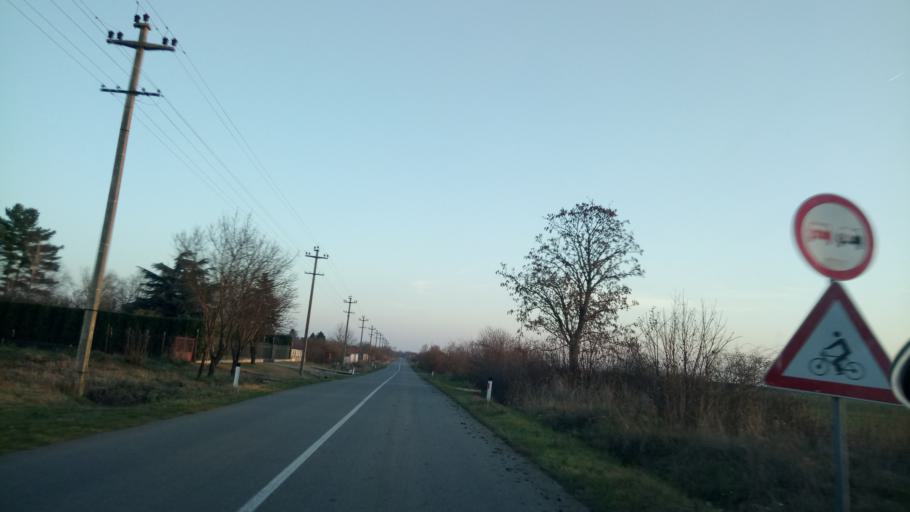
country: RS
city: Surduk
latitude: 45.0918
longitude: 20.2986
